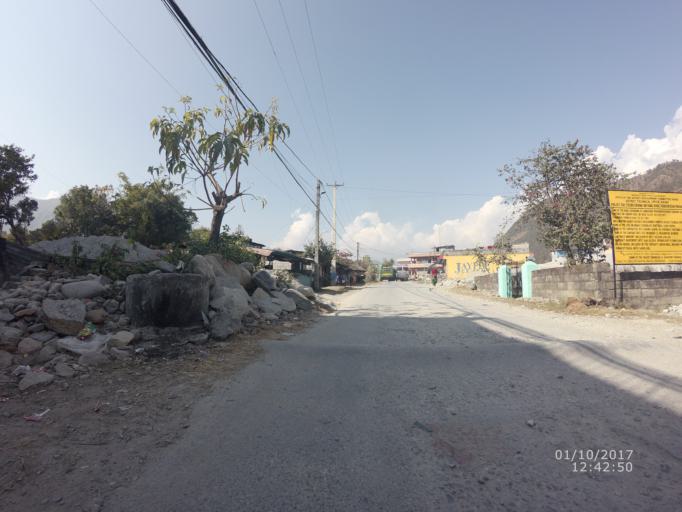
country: NP
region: Western Region
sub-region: Gandaki Zone
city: Pokhara
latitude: 28.2661
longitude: 83.9667
